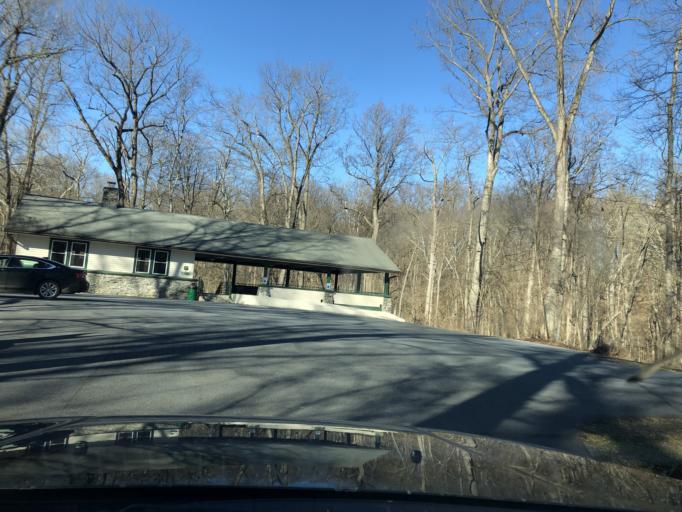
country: US
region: Pennsylvania
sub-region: Lancaster County
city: Lancaster
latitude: 40.0153
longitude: -76.2833
